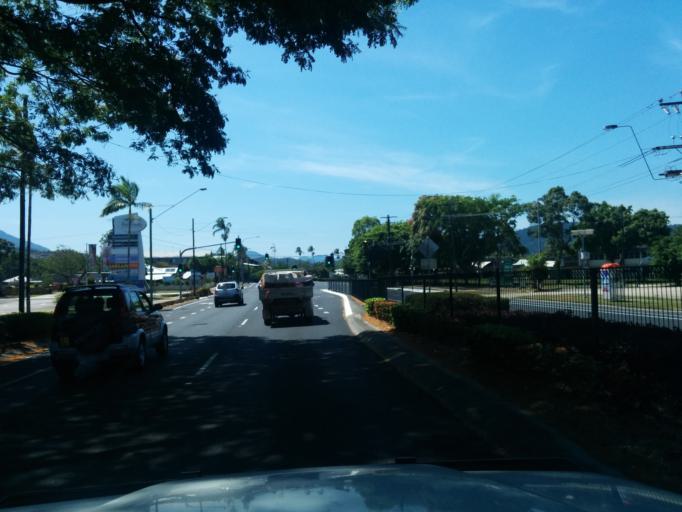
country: AU
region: Queensland
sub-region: Cairns
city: Cairns
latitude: -16.9257
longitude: 145.7414
